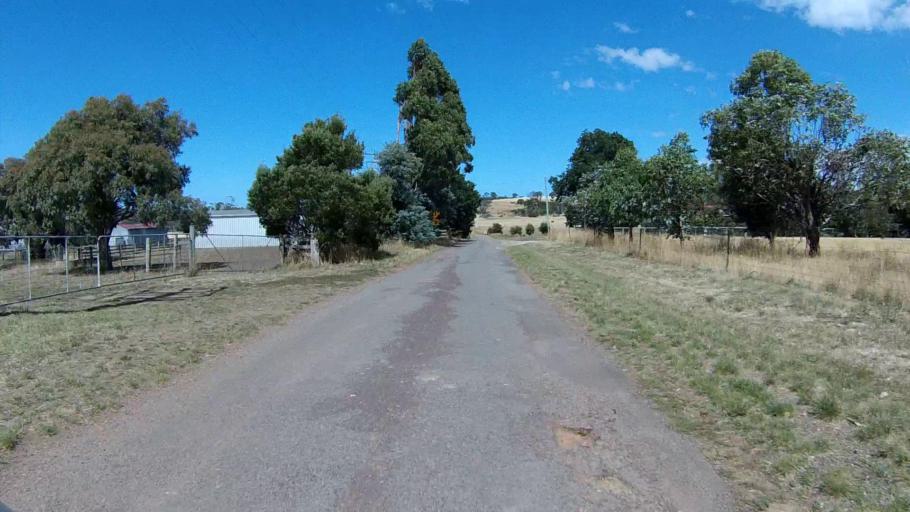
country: AU
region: Tasmania
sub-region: Break O'Day
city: St Helens
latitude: -41.9618
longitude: 148.0711
